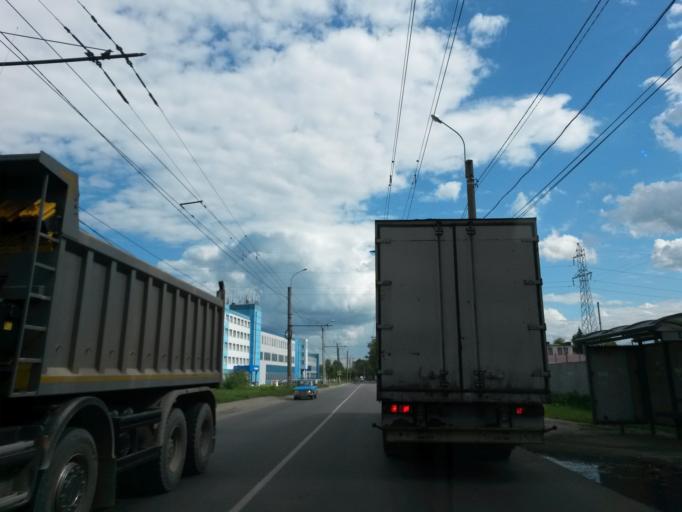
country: RU
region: Ivanovo
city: Novo-Talitsy
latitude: 56.9993
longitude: 40.9075
